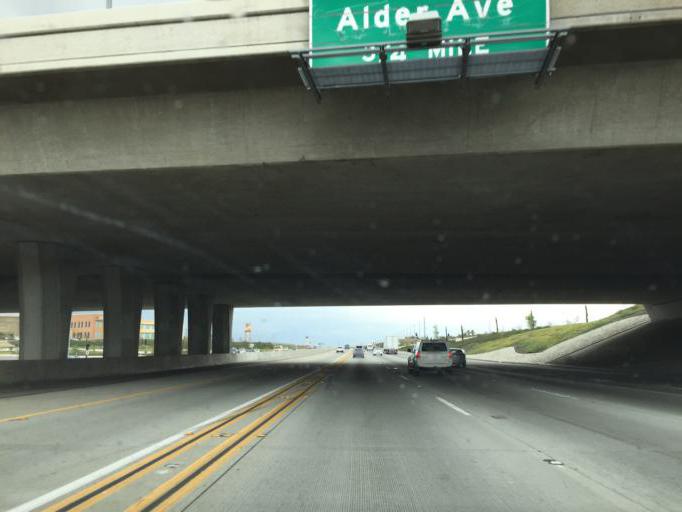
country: US
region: California
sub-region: San Bernardino County
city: Fontana
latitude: 34.1362
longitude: -117.4365
